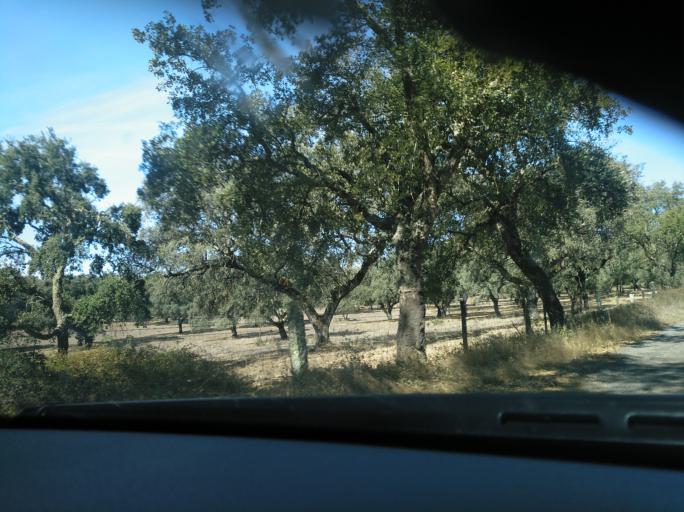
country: PT
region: Evora
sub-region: Arraiolos
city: Arraiolos
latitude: 38.6998
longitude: -8.0952
